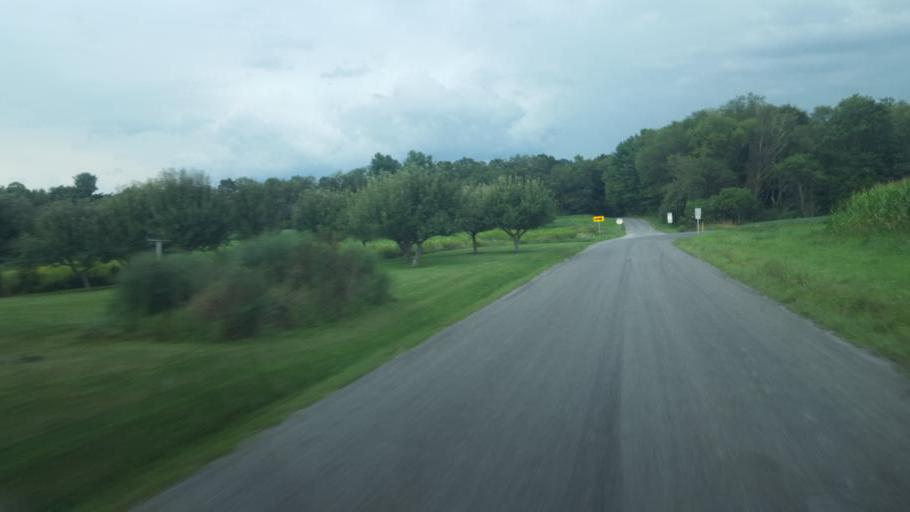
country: US
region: Pennsylvania
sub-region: Clarion County
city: Knox
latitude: 41.1734
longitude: -79.5297
